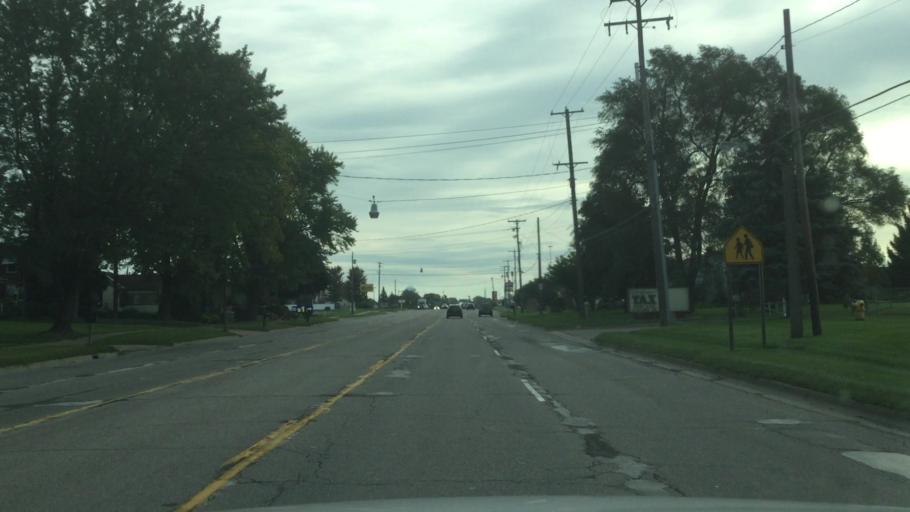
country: US
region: Michigan
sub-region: Genesee County
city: Flint
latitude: 42.9741
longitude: -83.6890
